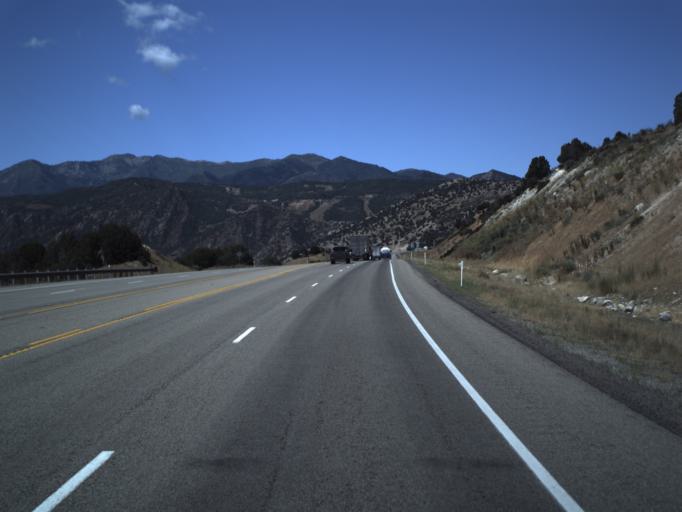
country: US
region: Utah
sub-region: Utah County
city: Mapleton
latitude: 39.9952
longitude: -111.4643
